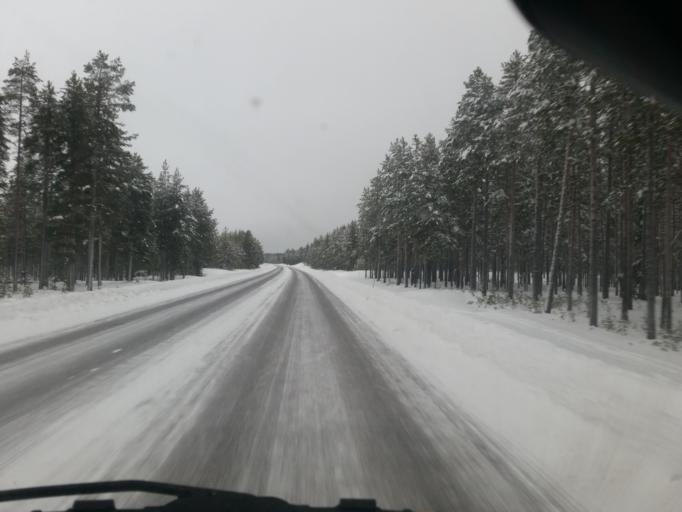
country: SE
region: Norrbotten
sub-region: Pitea Kommun
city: Pitea
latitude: 65.2423
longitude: 21.5307
